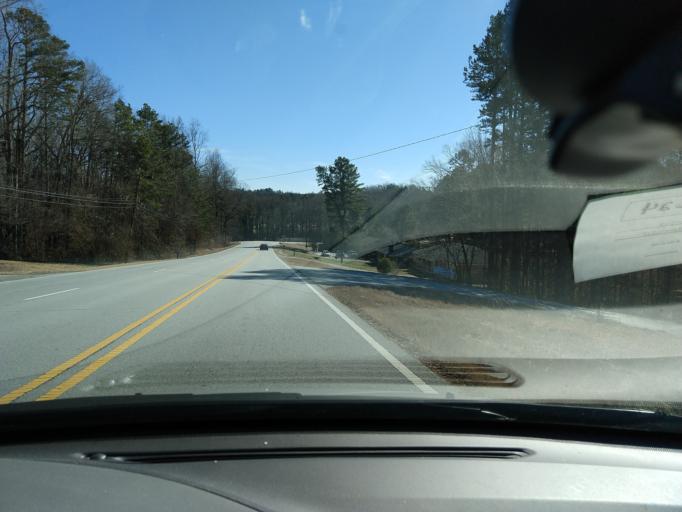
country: US
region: Georgia
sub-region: Stephens County
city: Toccoa
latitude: 34.5972
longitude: -83.3488
